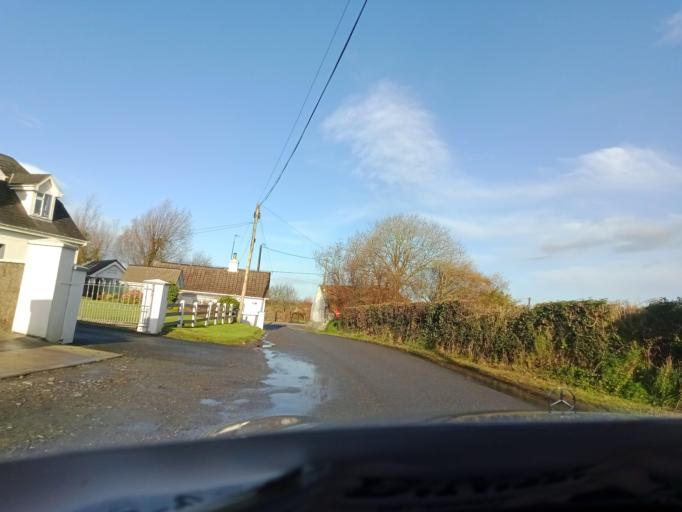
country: IE
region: Leinster
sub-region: Kilkenny
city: Mooncoin
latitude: 52.2738
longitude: -7.2330
